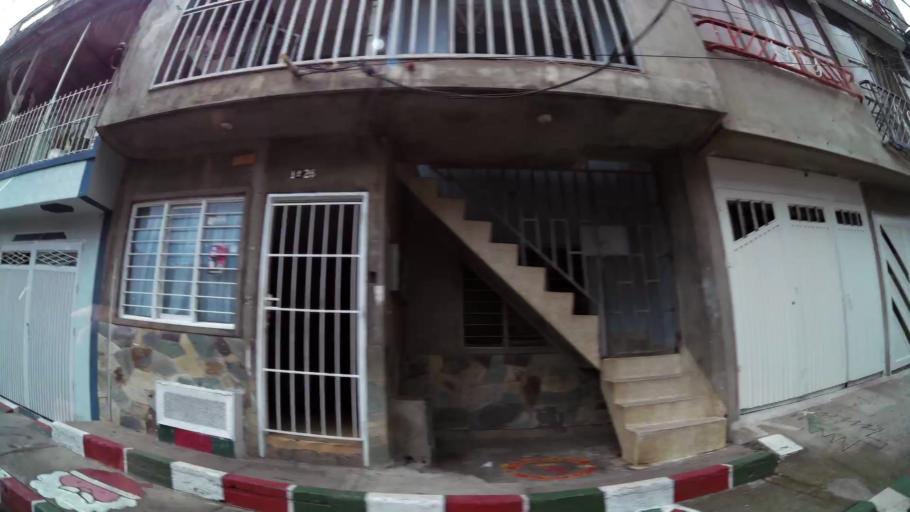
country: CO
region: Valle del Cauca
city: Cali
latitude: 3.3872
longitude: -76.5547
